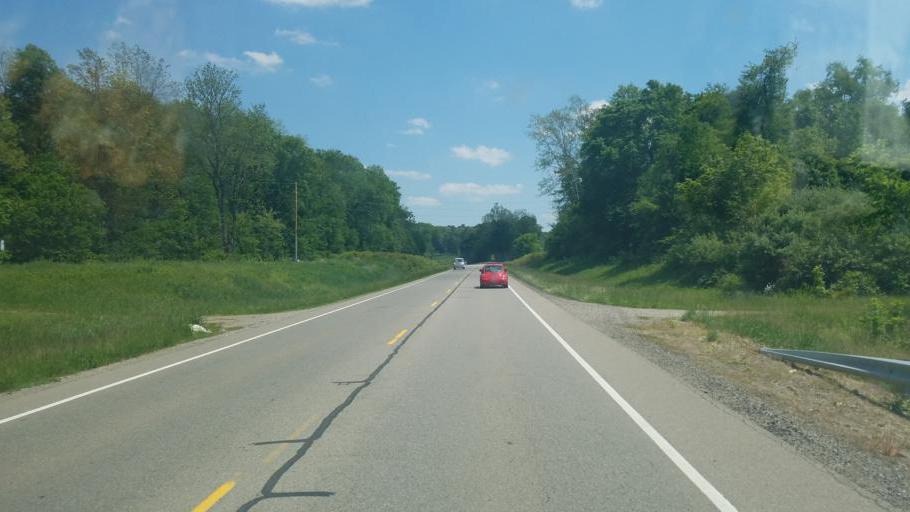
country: US
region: Ohio
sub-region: Muskingum County
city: Frazeysburg
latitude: 40.0538
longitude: -82.1354
